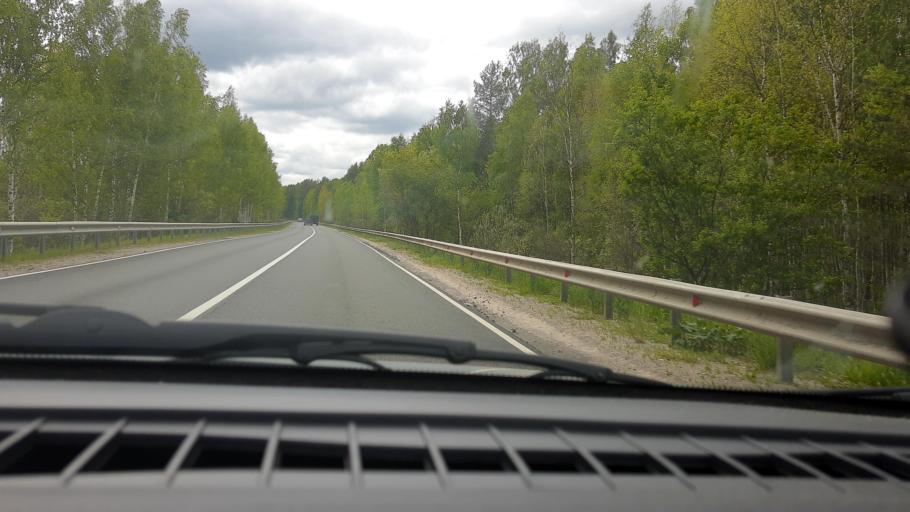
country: RU
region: Nizjnij Novgorod
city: Krasnyye Baki
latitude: 57.1354
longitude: 45.2164
